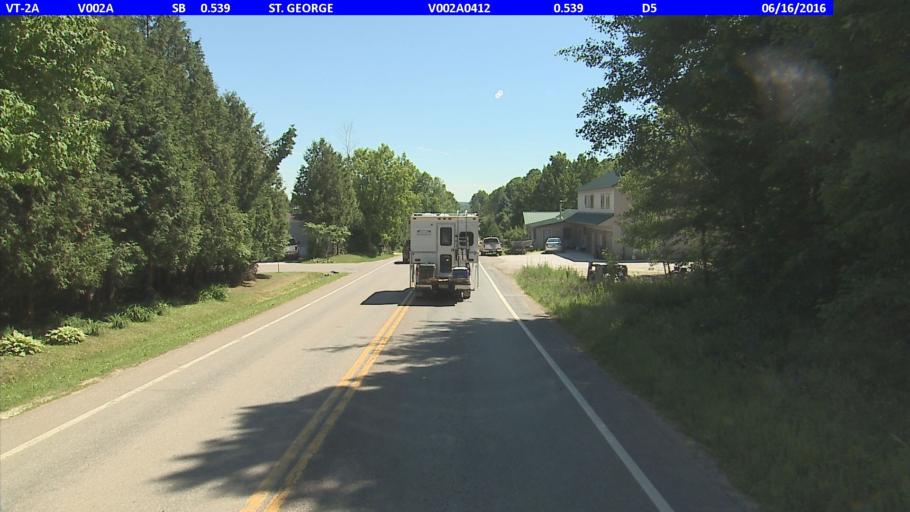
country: US
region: Vermont
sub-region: Chittenden County
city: Hinesburg
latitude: 44.3774
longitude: -73.1266
